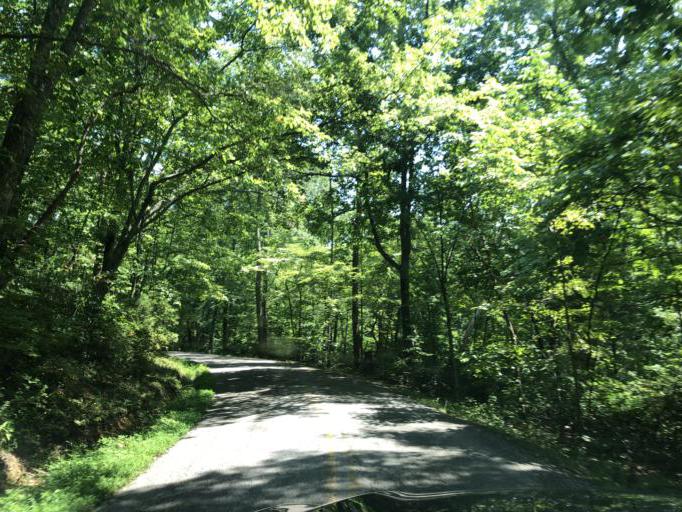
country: US
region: Tennessee
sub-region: Franklin County
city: Sewanee
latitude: 35.2024
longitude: -85.9315
